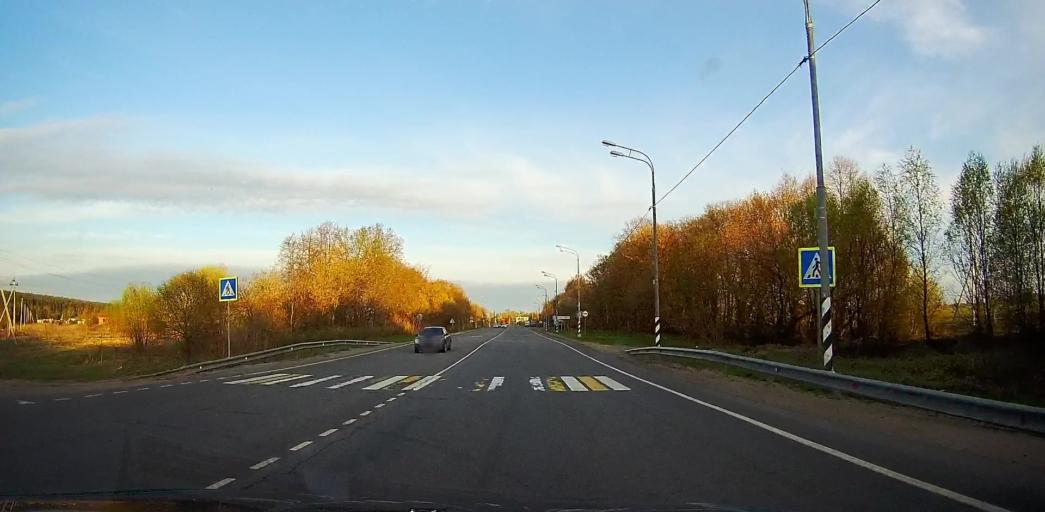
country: RU
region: Moskovskaya
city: Troitskoye
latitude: 55.2300
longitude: 38.5544
